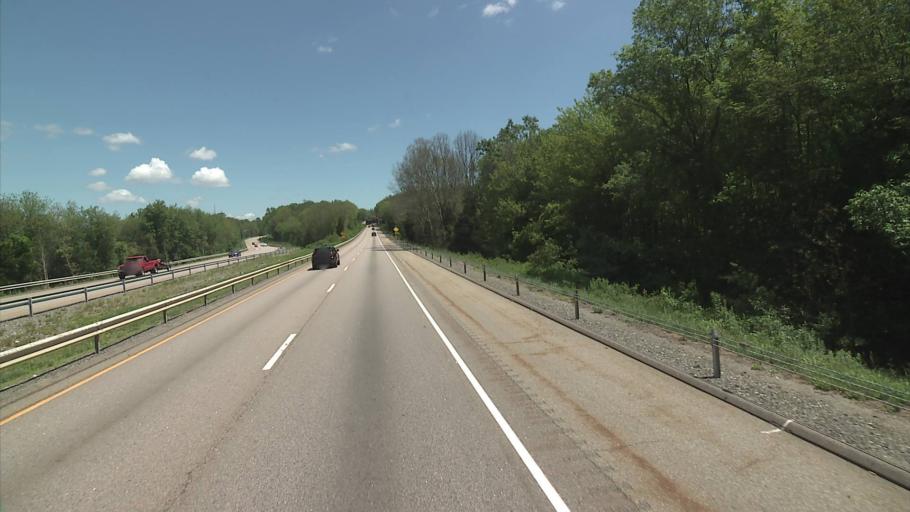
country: US
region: Connecticut
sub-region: New London County
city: Oxoboxo River
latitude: 41.4249
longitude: -72.1272
